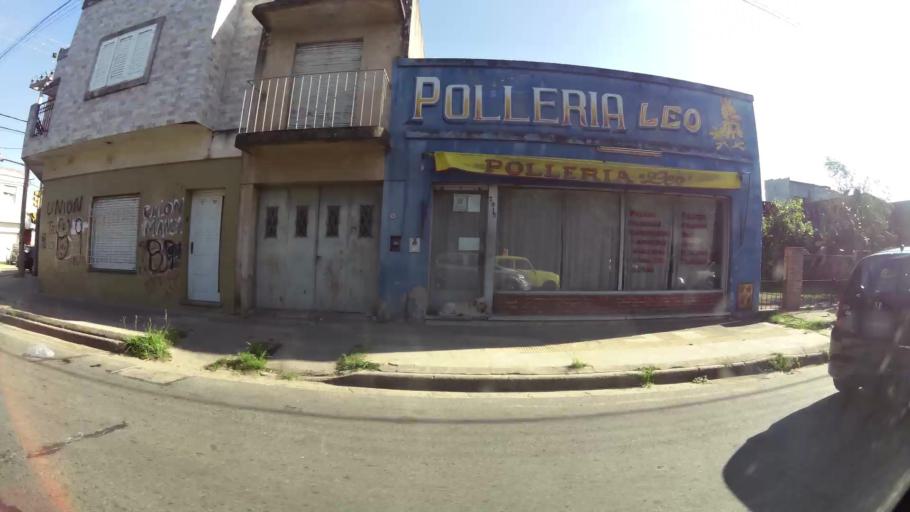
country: AR
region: Santa Fe
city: Santa Fe de la Vera Cruz
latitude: -31.6046
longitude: -60.6987
